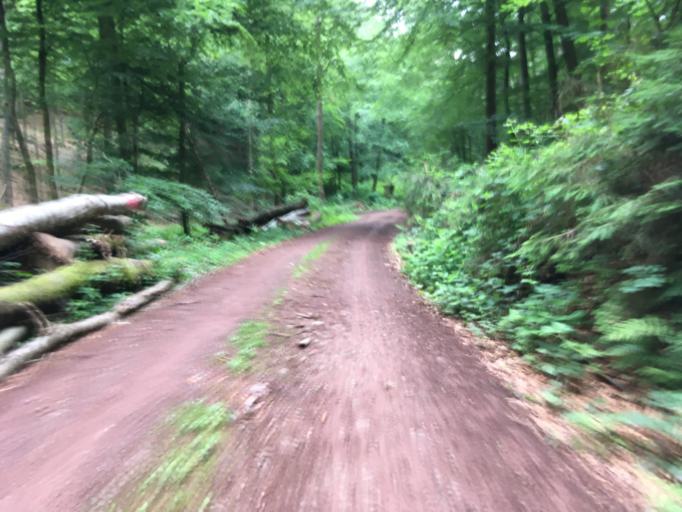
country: DE
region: Saarland
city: Britten
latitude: 49.5046
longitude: 6.6589
